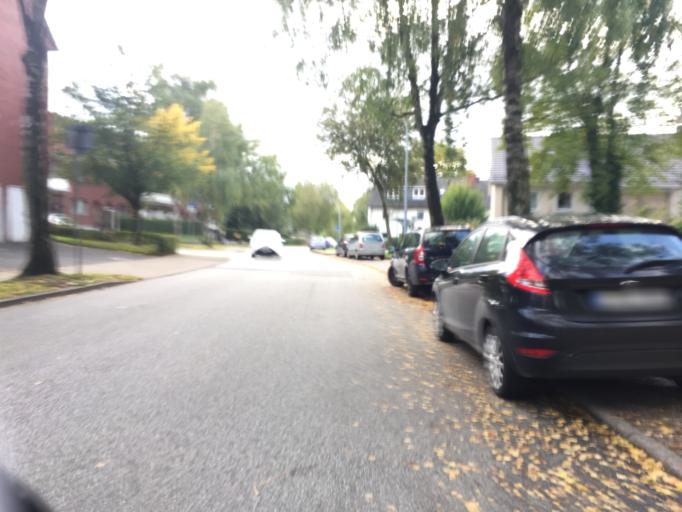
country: DE
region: Schleswig-Holstein
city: Itzehoe
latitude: 53.9415
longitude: 9.5081
